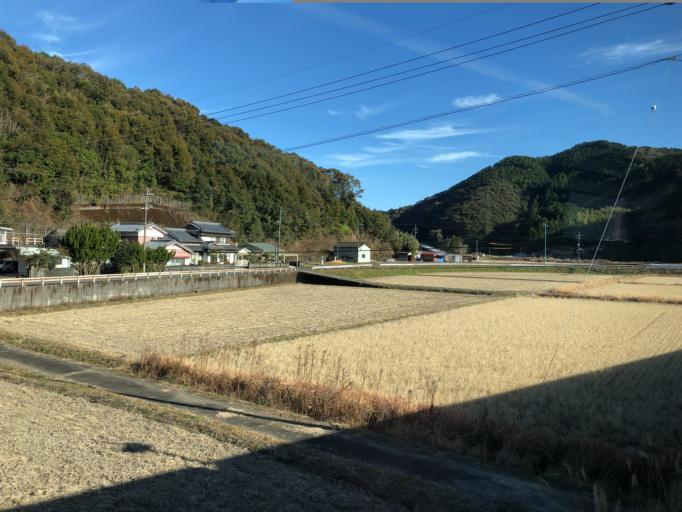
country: JP
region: Kochi
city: Nakamura
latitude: 33.1013
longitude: 133.0991
